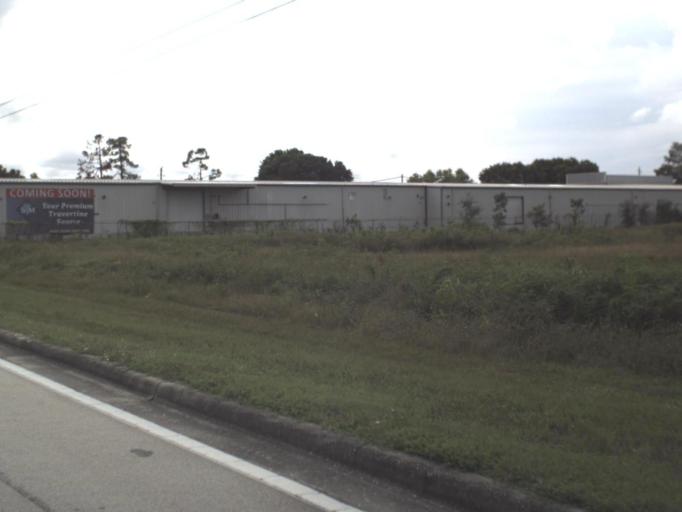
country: US
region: Florida
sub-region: Lee County
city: Pine Manor
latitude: 26.5871
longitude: -81.8534
